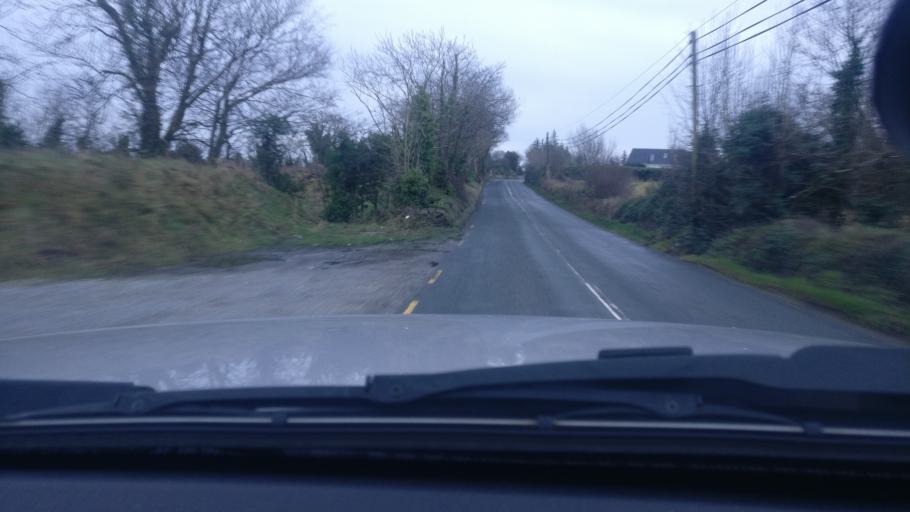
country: IE
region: Connaught
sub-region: County Galway
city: Loughrea
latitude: 53.1700
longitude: -8.5233
